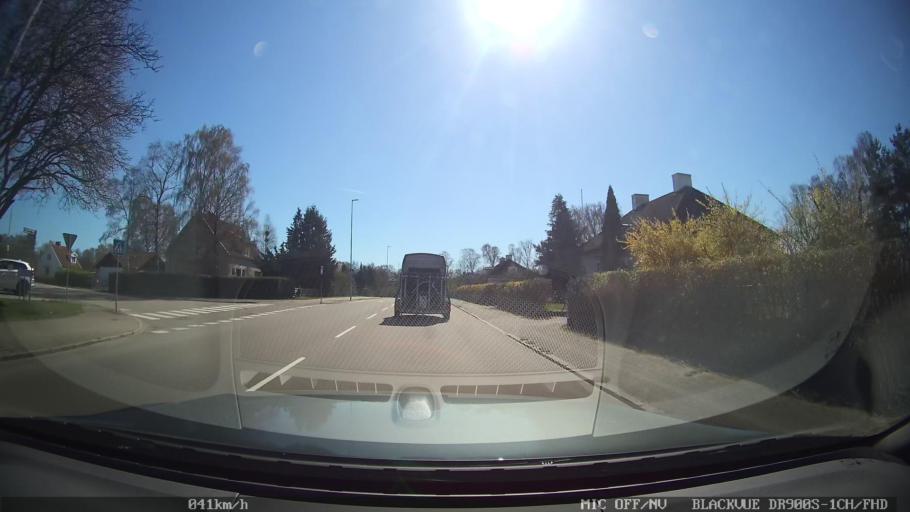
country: SE
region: Skane
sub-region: Klippans Kommun
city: Ljungbyhed
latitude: 56.0790
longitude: 13.2365
